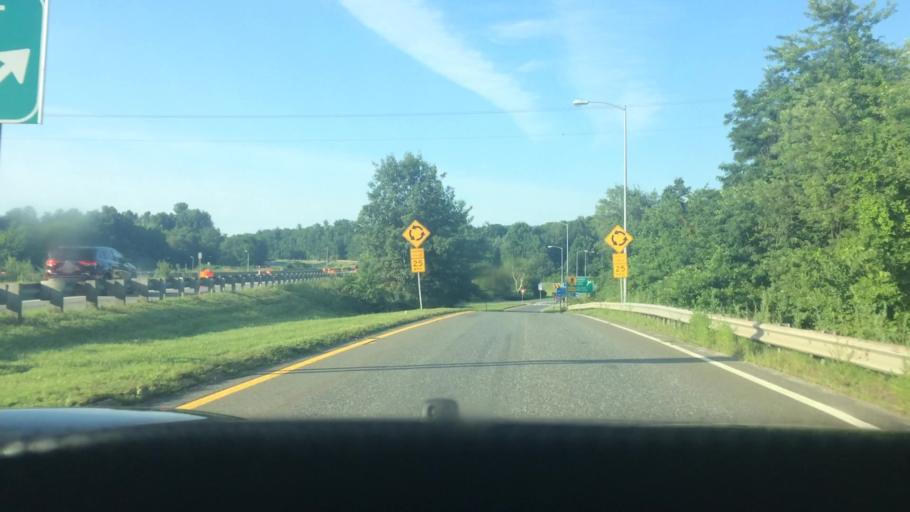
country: US
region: Massachusetts
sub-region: Franklin County
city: Greenfield
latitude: 42.5875
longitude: -72.6212
